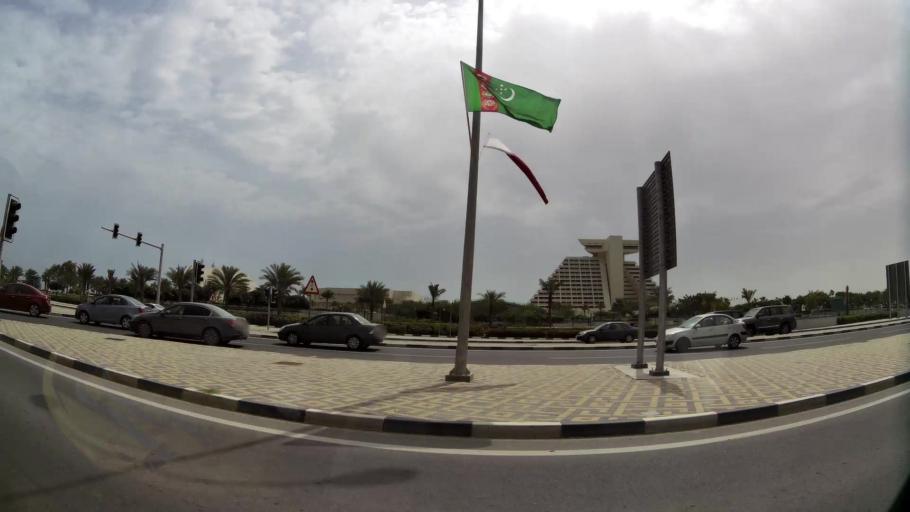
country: QA
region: Baladiyat ad Dawhah
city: Doha
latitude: 25.3214
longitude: 51.5342
